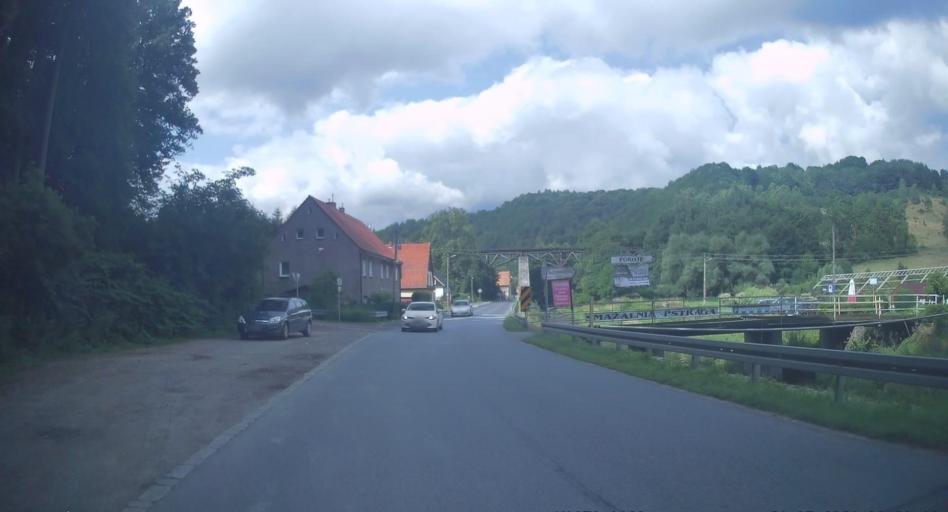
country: PL
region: Lower Silesian Voivodeship
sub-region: Powiat walbrzyski
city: Walim
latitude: 50.7408
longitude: 16.4106
